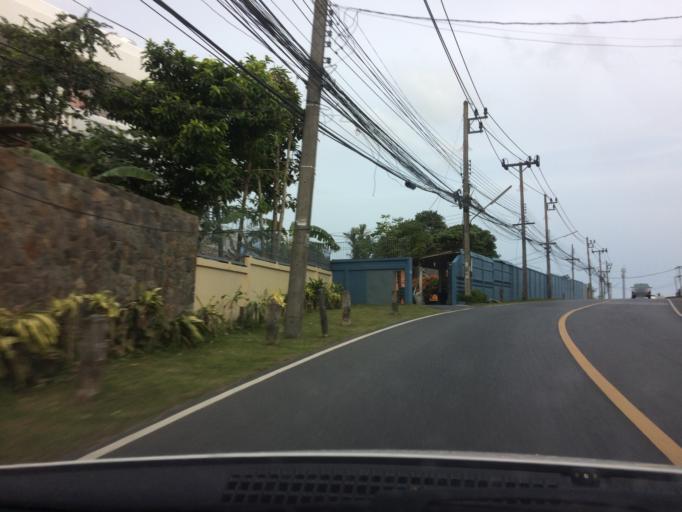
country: TH
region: Phuket
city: Ban Ratsada
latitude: 7.9029
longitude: 98.4103
